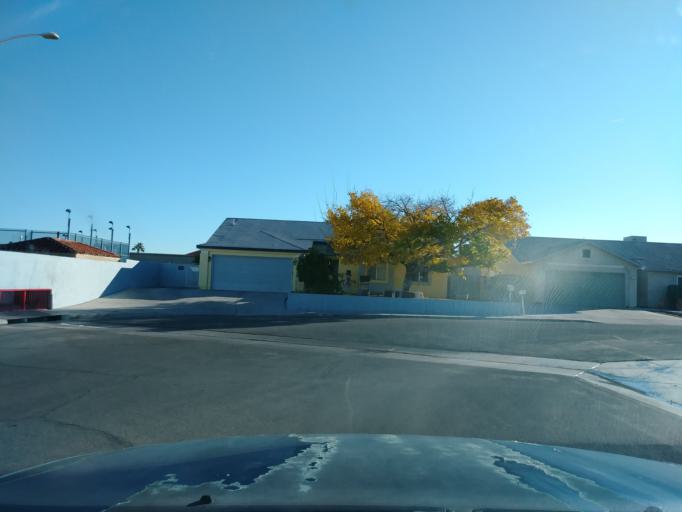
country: US
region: Nevada
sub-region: Clark County
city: Spring Valley
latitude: 36.1616
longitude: -115.2467
